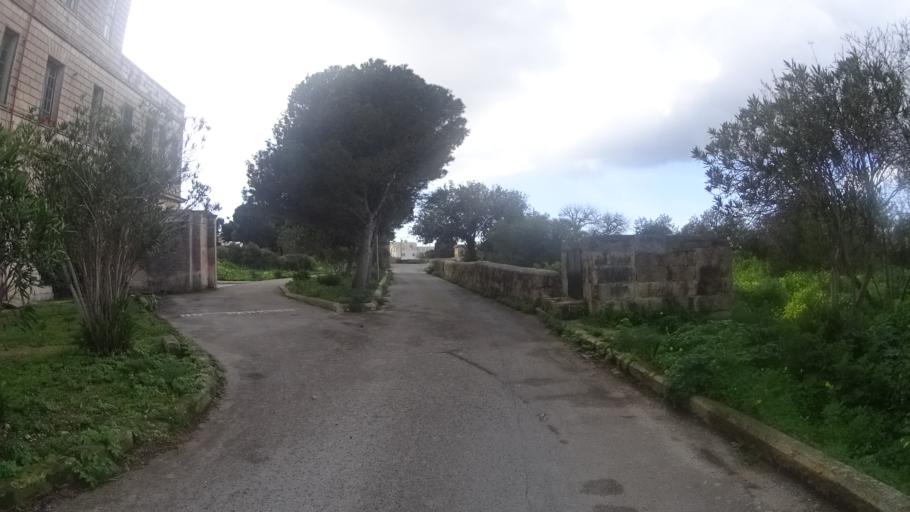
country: MT
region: L-Imtarfa
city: Imtarfa
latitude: 35.8909
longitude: 14.3951
